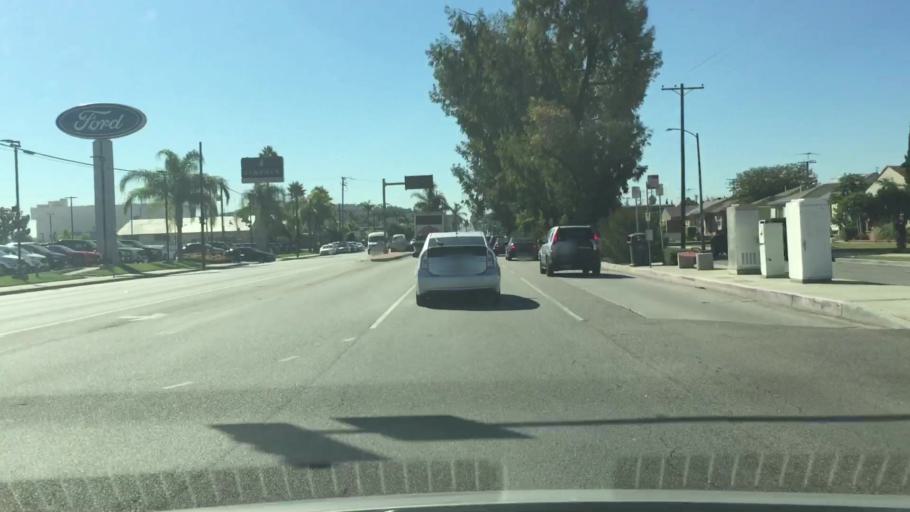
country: US
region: California
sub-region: Los Angeles County
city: Signal Hill
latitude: 33.8220
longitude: -118.1676
